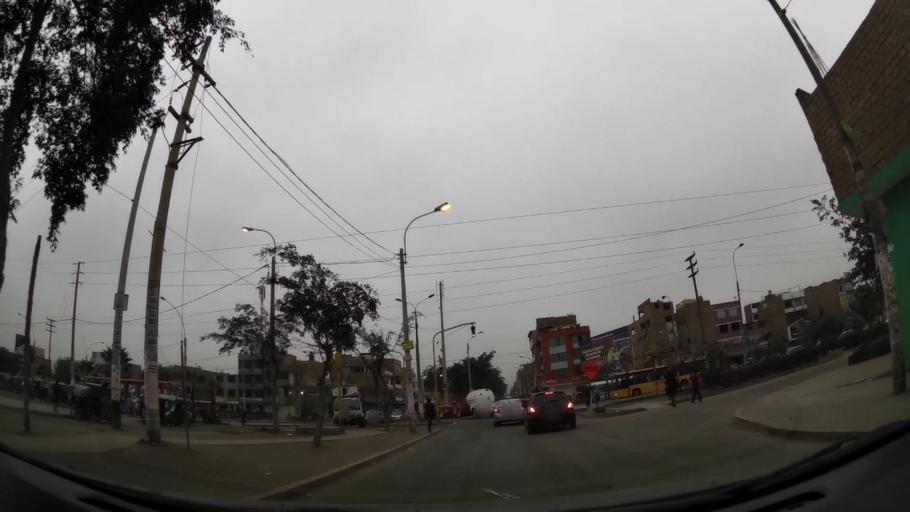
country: PE
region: Lima
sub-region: Lima
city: Urb. Santo Domingo
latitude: -11.9152
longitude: -77.0476
